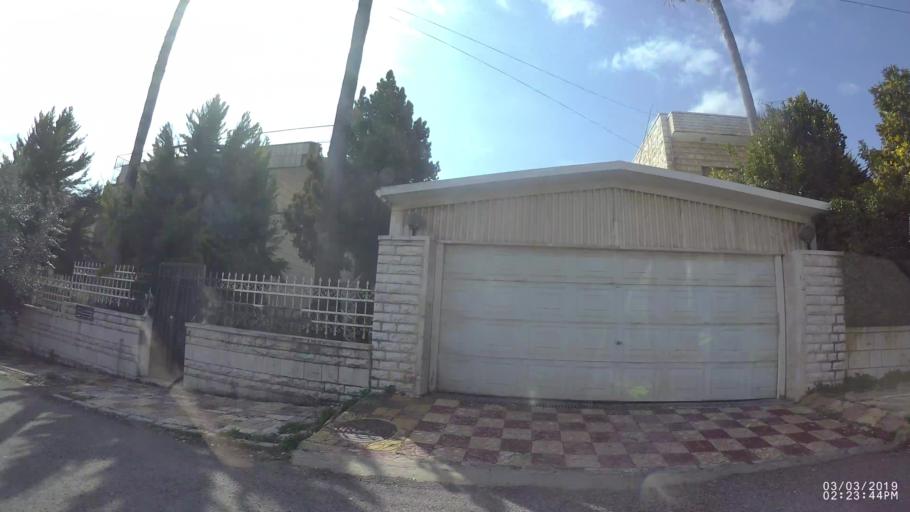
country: JO
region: Amman
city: Amman
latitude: 31.9693
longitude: 35.8900
